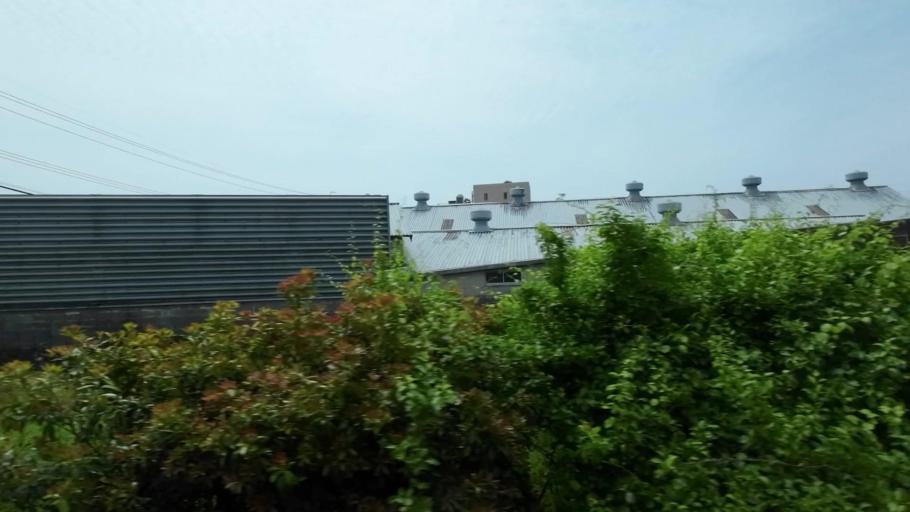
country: JP
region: Kochi
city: Kochi-shi
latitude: 33.5783
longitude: 133.6356
